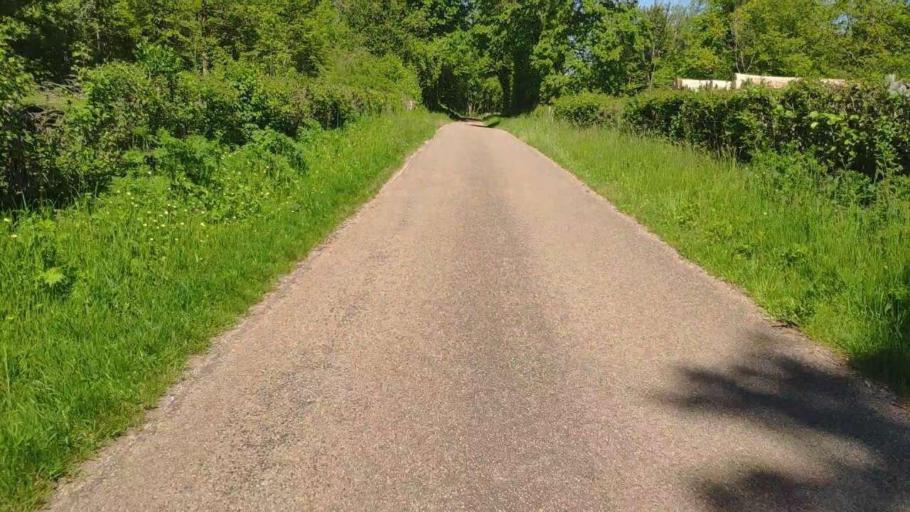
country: FR
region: Franche-Comte
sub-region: Departement du Jura
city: Poligny
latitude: 46.7326
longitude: 5.7345
